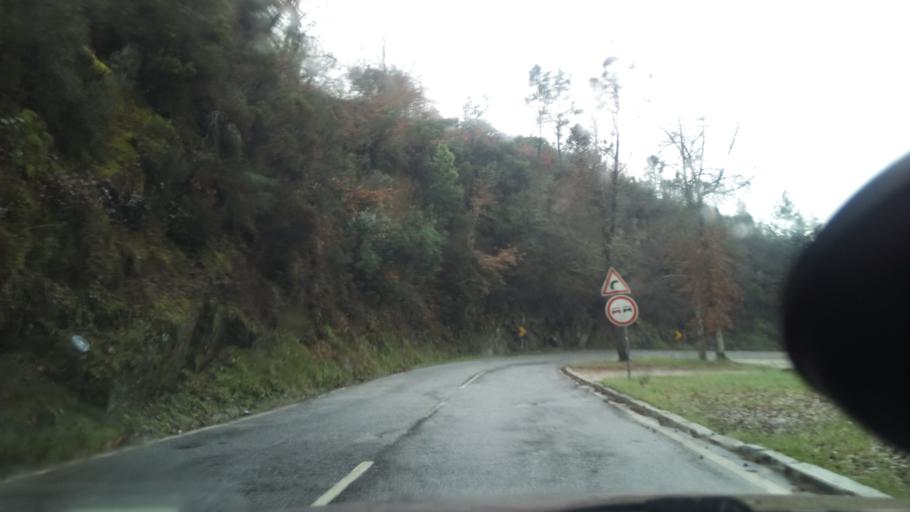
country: PT
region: Viseu
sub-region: Mangualde
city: Mangualde
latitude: 40.6341
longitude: -7.8192
